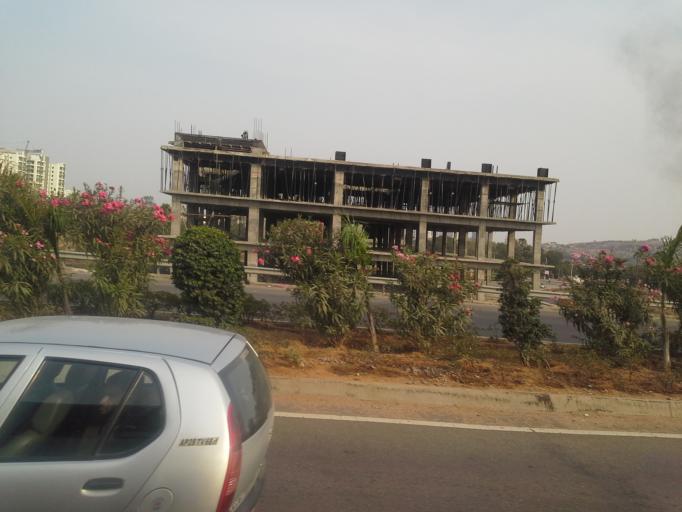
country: IN
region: Telangana
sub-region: Rangareddi
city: Kukatpalli
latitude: 17.4195
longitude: 78.3564
